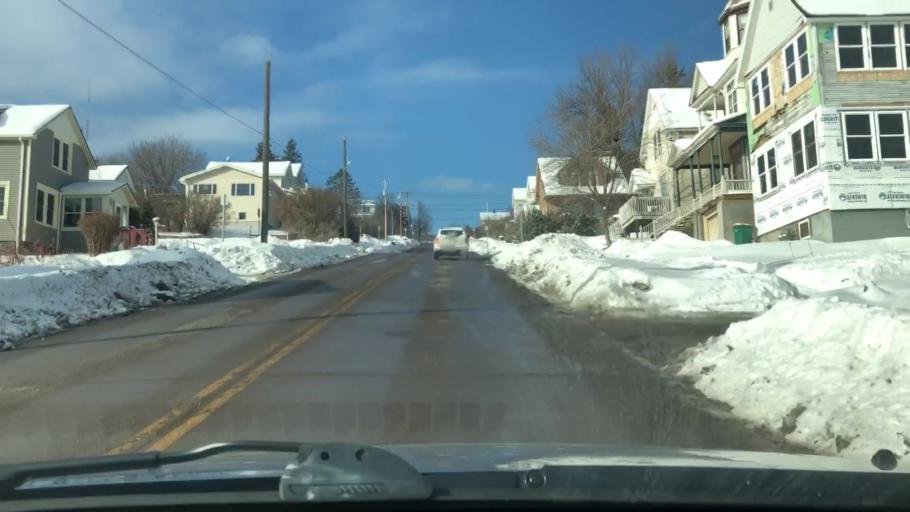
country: US
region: Minnesota
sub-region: Saint Louis County
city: Duluth
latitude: 46.7906
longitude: -92.1041
